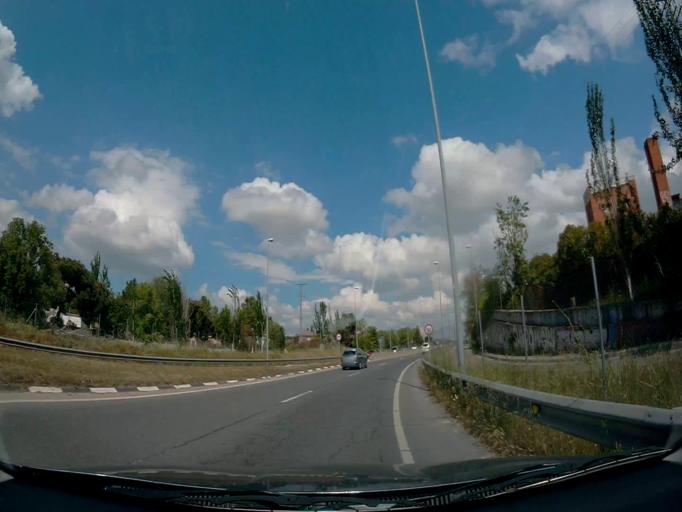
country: ES
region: Madrid
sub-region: Provincia de Madrid
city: Villaviciosa de Odon
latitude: 40.3517
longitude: -3.8912
